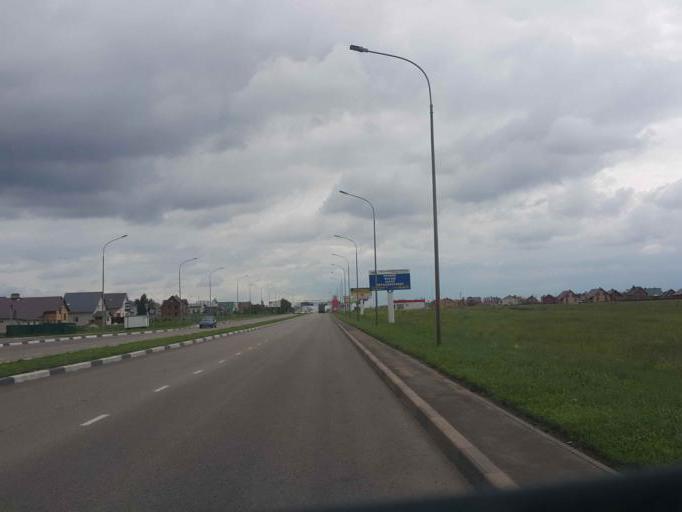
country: RU
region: Tambov
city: Komsomolets
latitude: 52.7837
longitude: 41.3723
